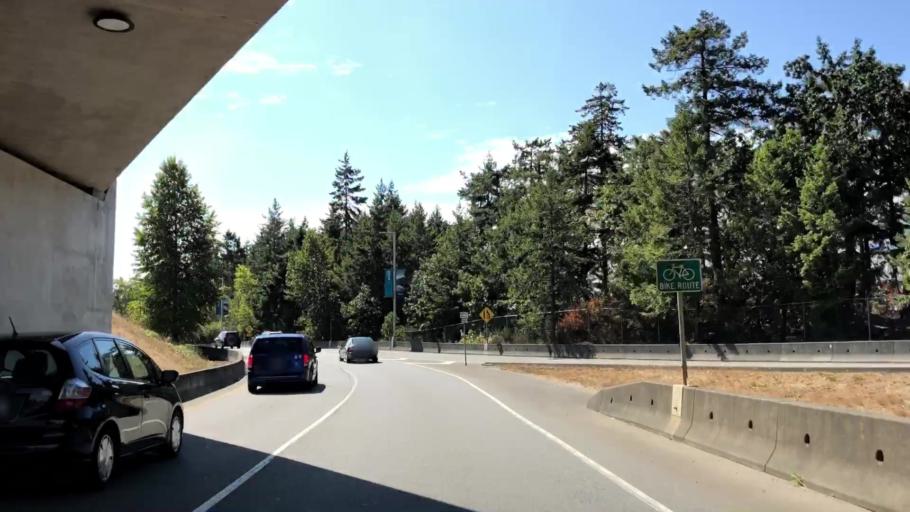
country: CA
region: British Columbia
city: Nanaimo
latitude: 49.1585
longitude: -123.8918
